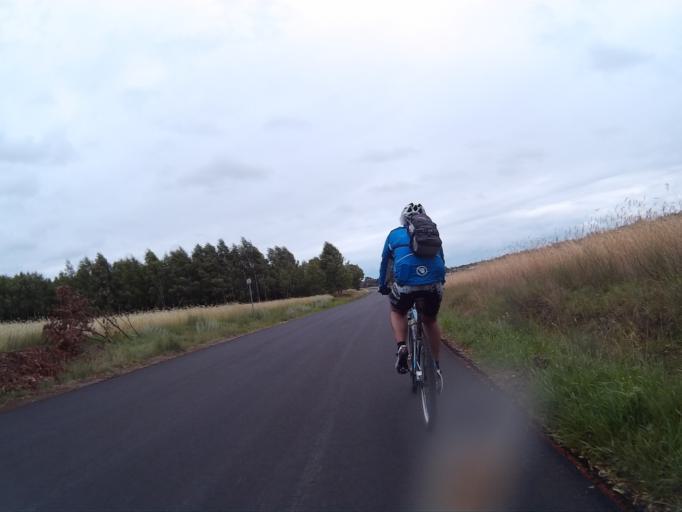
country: PL
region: Kujawsko-Pomorskie
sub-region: Powiat swiecki
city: Lniano
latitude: 53.6034
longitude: 18.2039
